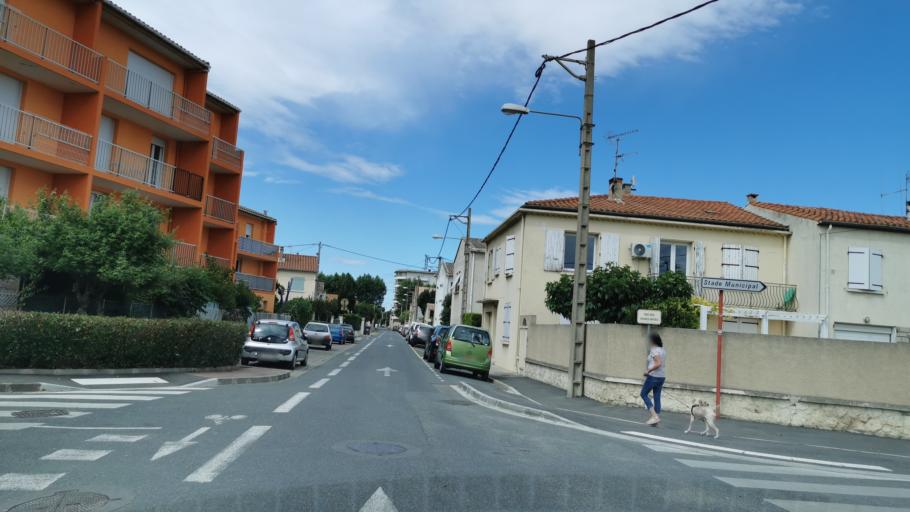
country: FR
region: Languedoc-Roussillon
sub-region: Departement de l'Aude
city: Narbonne
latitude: 43.1900
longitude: 3.0135
